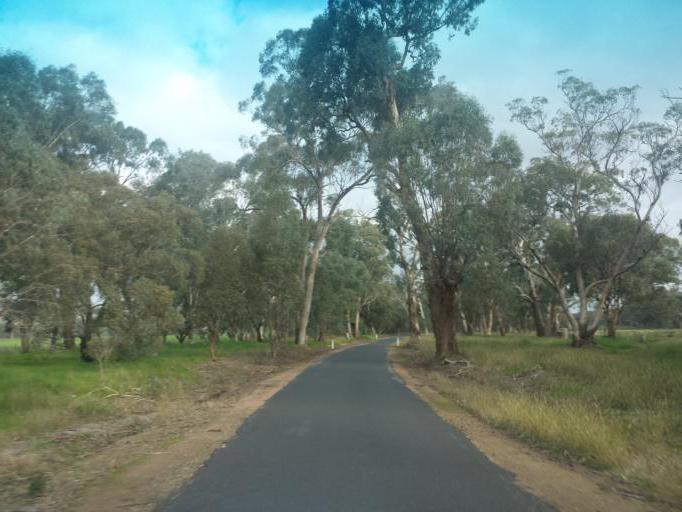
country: AU
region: Victoria
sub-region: Murrindindi
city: Kinglake West
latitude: -36.9193
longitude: 145.2256
